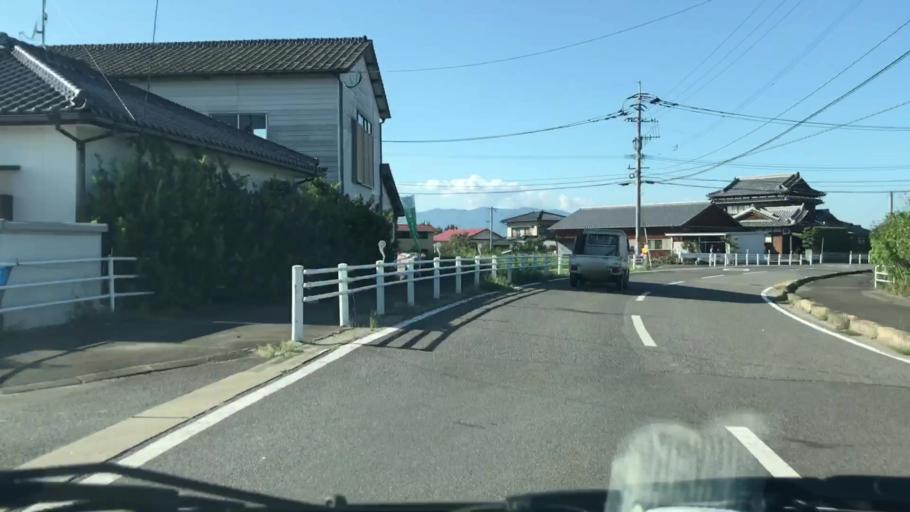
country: JP
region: Saga Prefecture
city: Saga-shi
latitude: 33.2014
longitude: 130.2656
